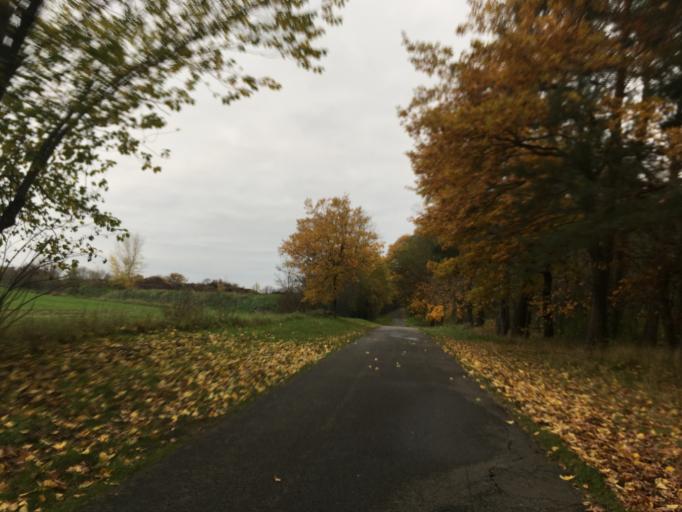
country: DE
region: Brandenburg
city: Frankfurt (Oder)
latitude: 52.3000
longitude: 14.5244
